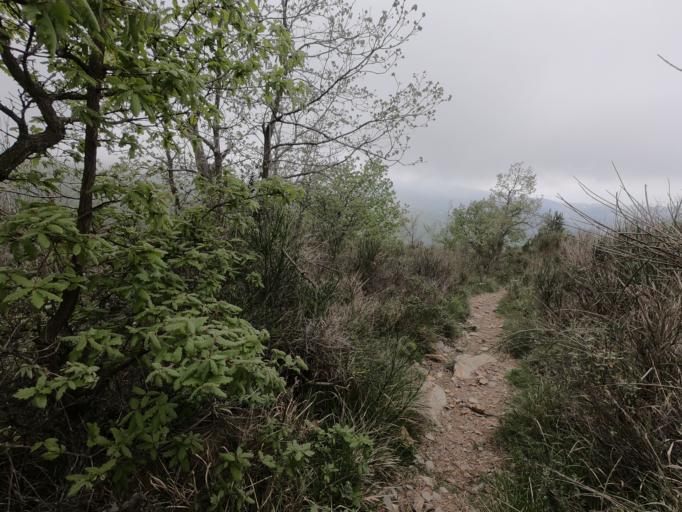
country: IT
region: Liguria
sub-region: Provincia di Imperia
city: Villa Faraldi
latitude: 43.9742
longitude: 8.0878
